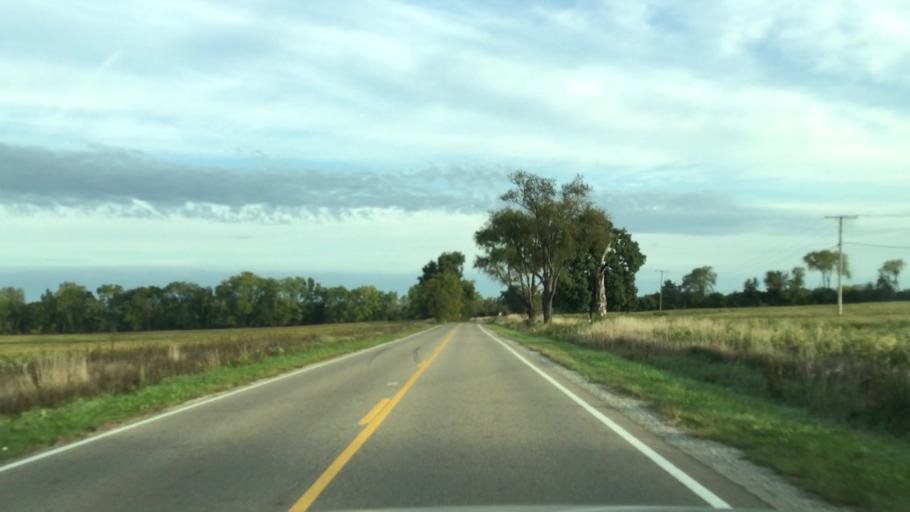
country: US
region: Michigan
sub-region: Livingston County
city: Whitmore Lake
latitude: 42.4321
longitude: -83.7759
